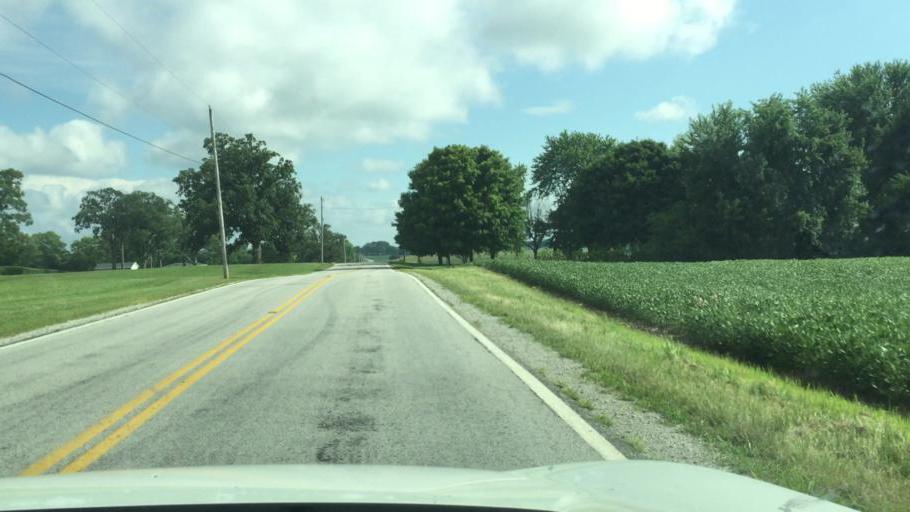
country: US
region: Ohio
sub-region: Clark County
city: Northridge
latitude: 39.9560
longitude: -83.6804
